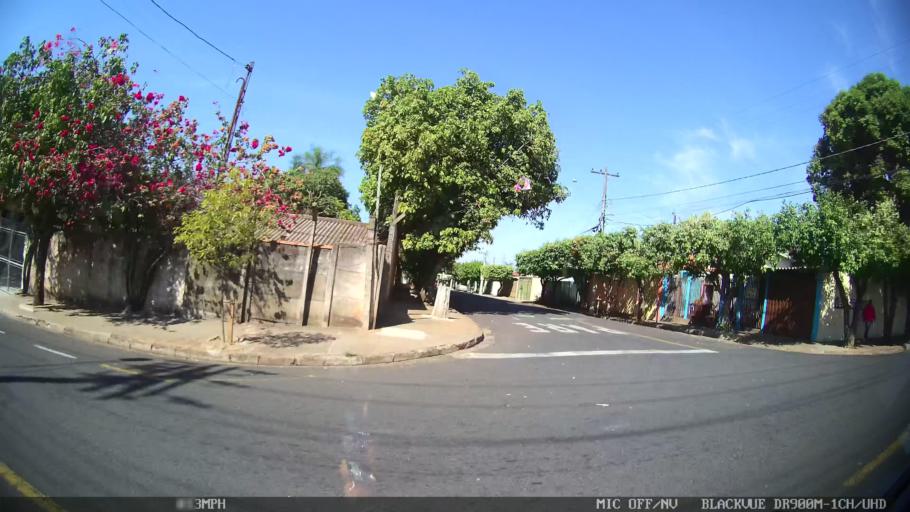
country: BR
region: Sao Paulo
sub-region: Sao Jose Do Rio Preto
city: Sao Jose do Rio Preto
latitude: -20.7782
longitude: -49.4056
